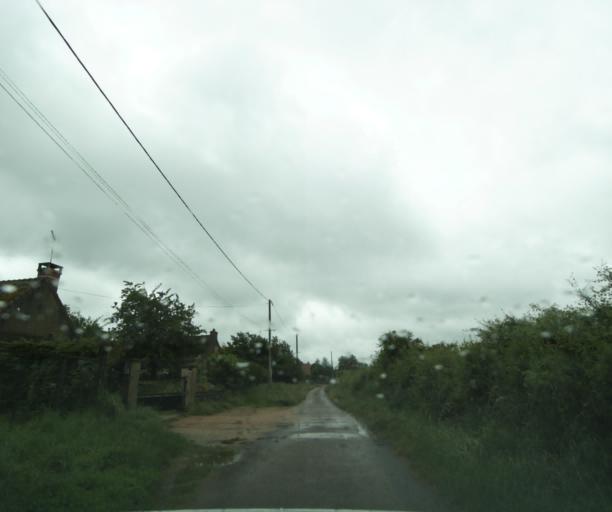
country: FR
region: Bourgogne
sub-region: Departement de Saone-et-Loire
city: Charolles
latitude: 46.4967
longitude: 4.3565
